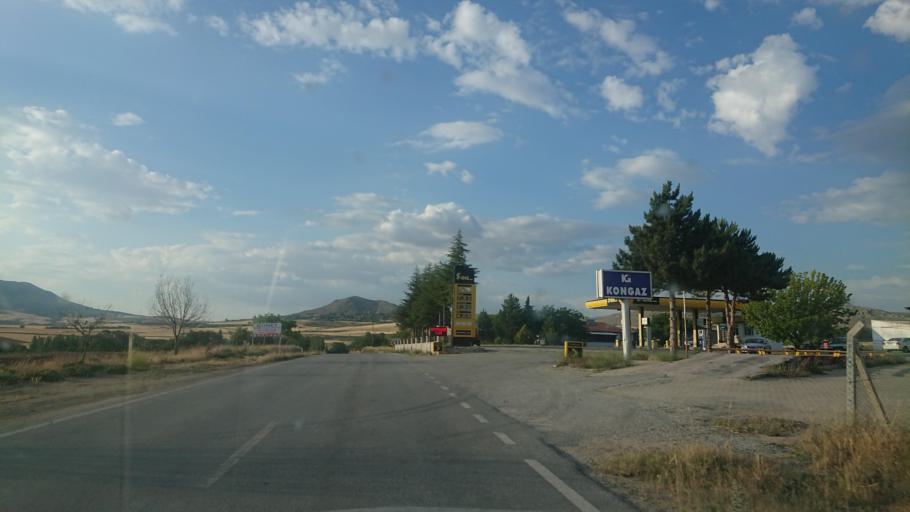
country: TR
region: Aksaray
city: Balci
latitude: 38.5672
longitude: 34.1053
